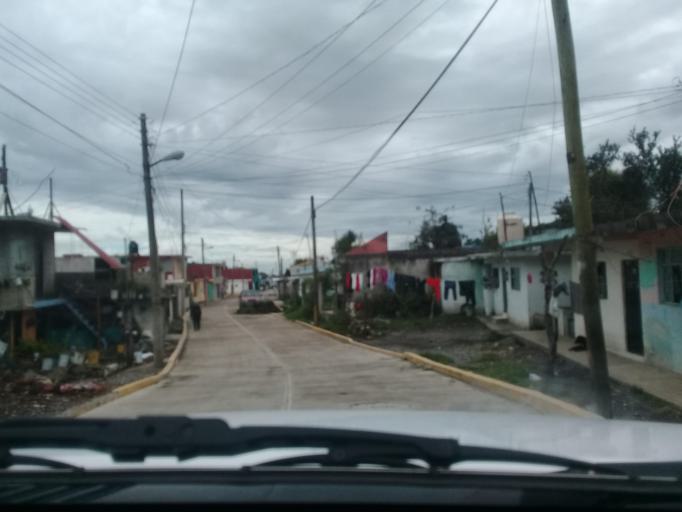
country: MX
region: Veracruz
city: Rafael Lucio
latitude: 19.5941
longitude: -96.9880
